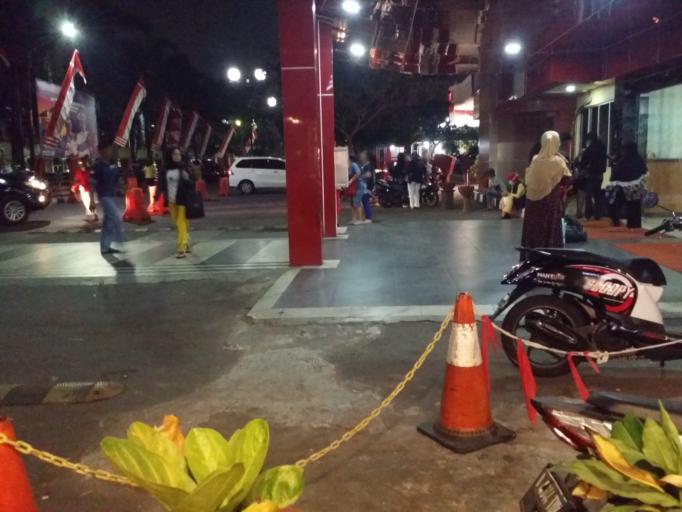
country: ID
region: Jakarta Raya
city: Jakarta
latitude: -6.2691
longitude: 106.8704
